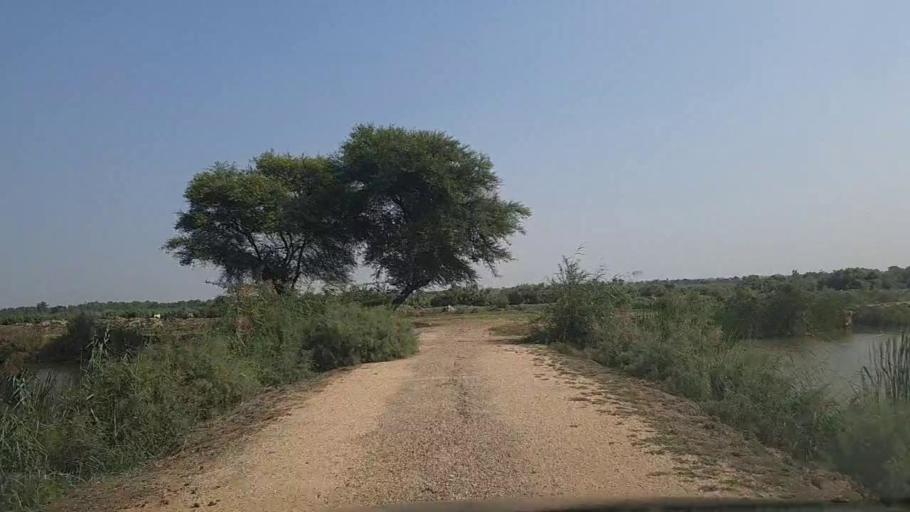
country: PK
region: Sindh
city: Thatta
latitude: 24.6231
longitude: 67.7938
